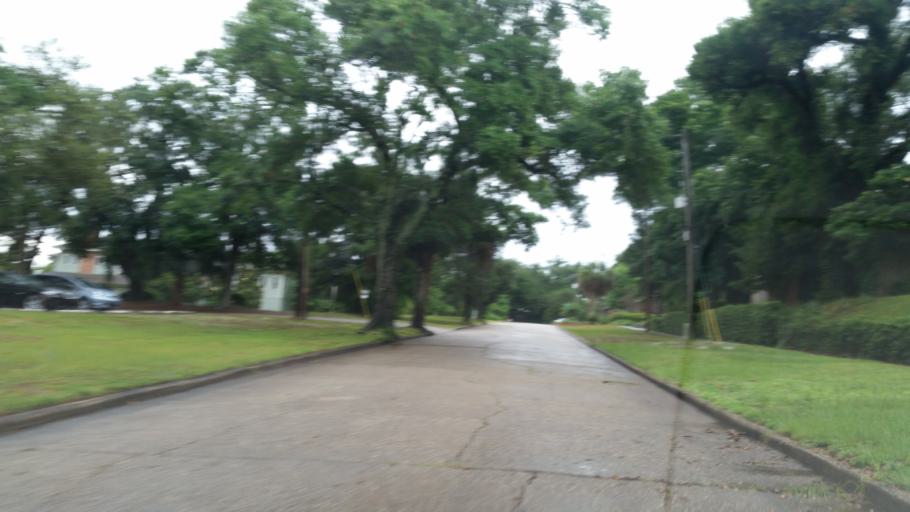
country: US
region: Florida
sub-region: Escambia County
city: East Pensacola Heights
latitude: 30.4249
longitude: -87.1906
